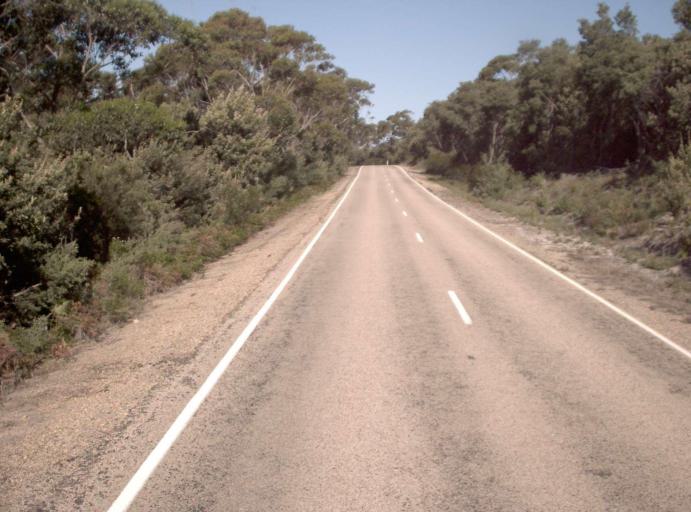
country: AU
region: Victoria
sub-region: East Gippsland
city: Lakes Entrance
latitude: -37.7981
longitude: 148.6900
